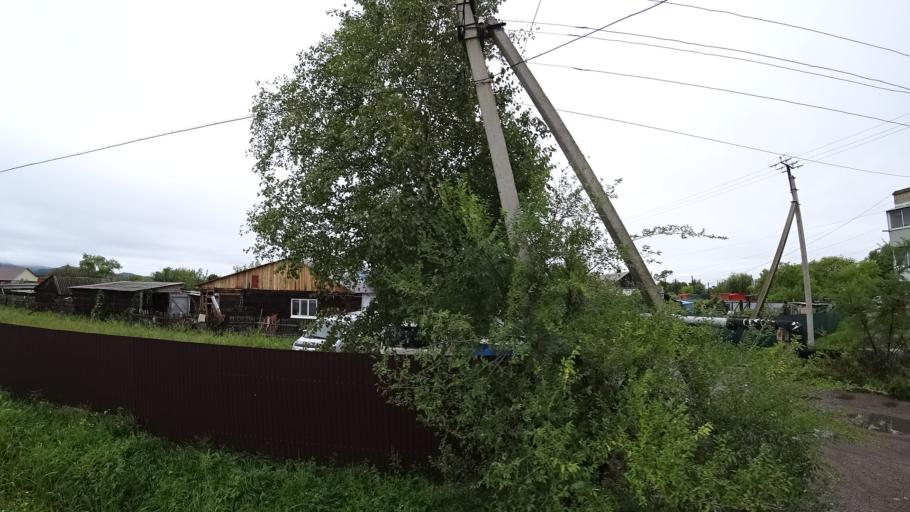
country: RU
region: Primorskiy
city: Monastyrishche
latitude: 44.2001
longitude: 132.4963
